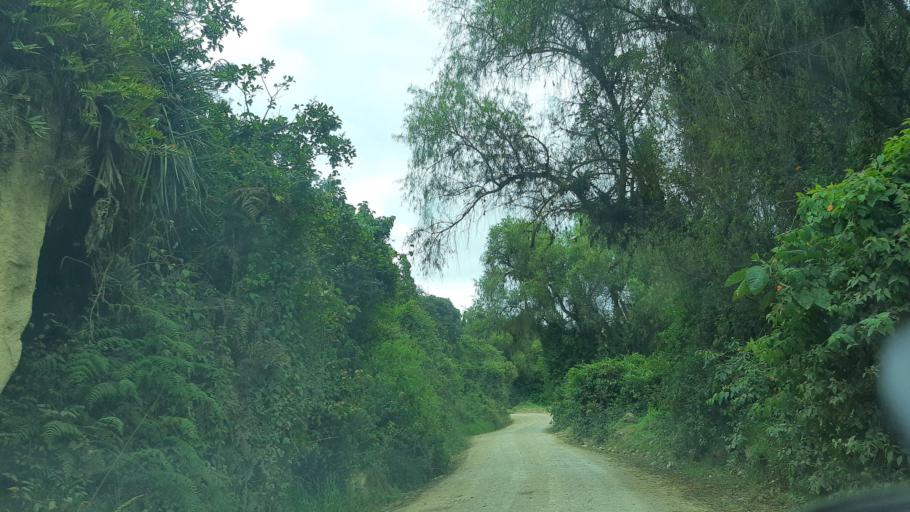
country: CO
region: Boyaca
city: Turmeque
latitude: 5.3362
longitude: -73.4609
